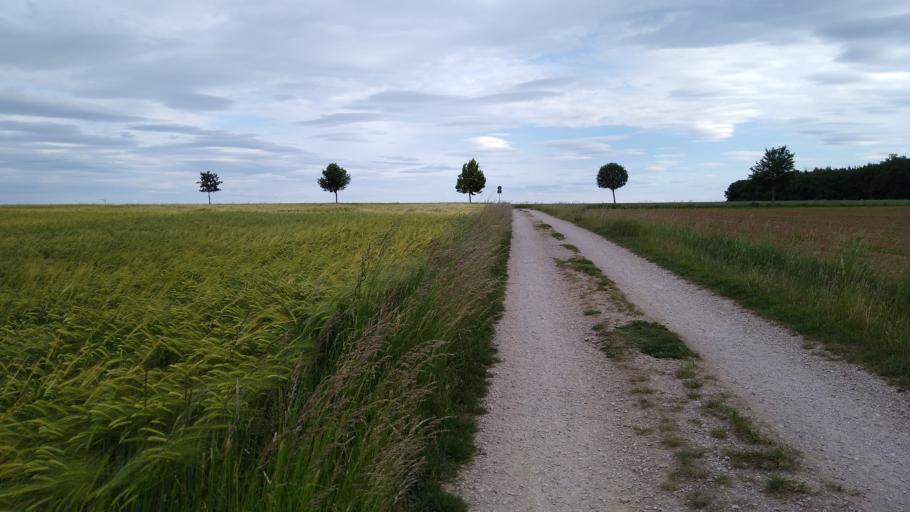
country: DE
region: Bavaria
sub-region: Regierungsbezirk Mittelfranken
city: Obermichelbach
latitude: 49.5300
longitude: 10.8944
